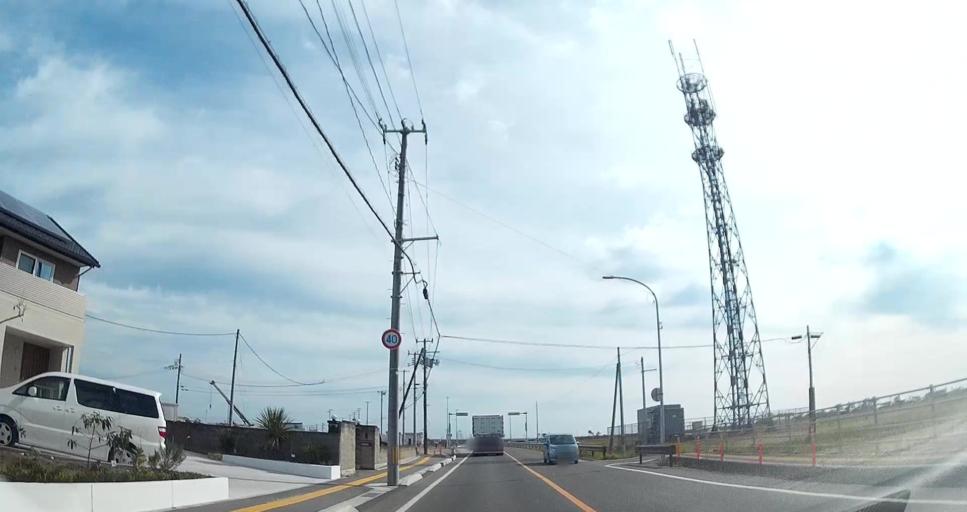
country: JP
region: Miyagi
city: Sendai
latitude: 38.1997
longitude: 140.9508
